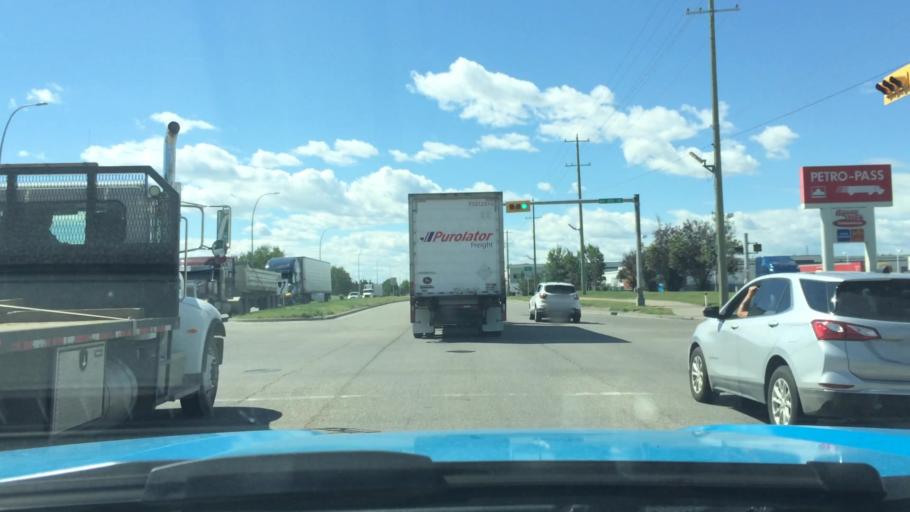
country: CA
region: Alberta
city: Calgary
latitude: 50.9993
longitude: -113.9587
